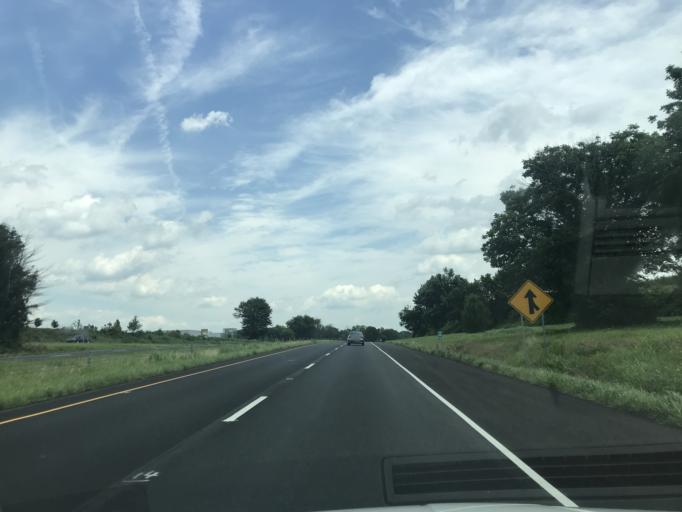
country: US
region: Pennsylvania
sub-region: Chester County
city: West Grove
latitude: 39.8270
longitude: -75.8695
